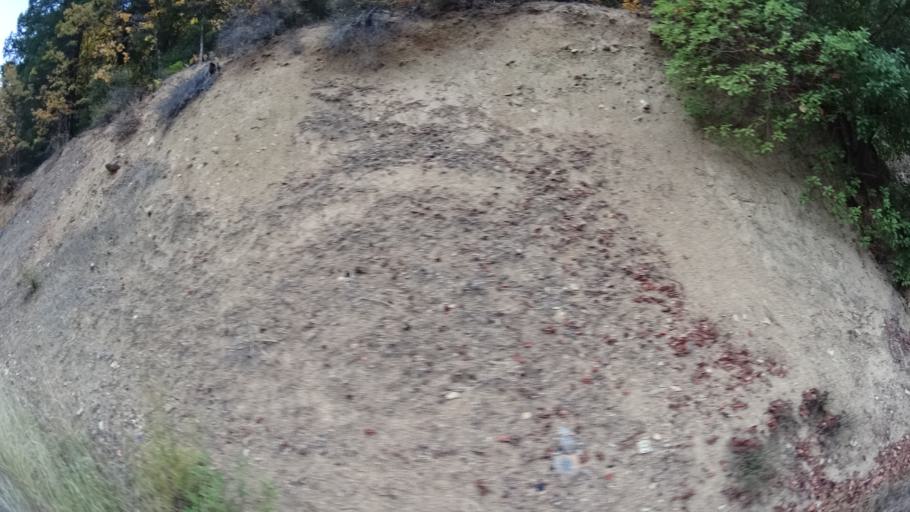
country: US
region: California
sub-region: Siskiyou County
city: Happy Camp
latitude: 41.9115
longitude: -123.4528
